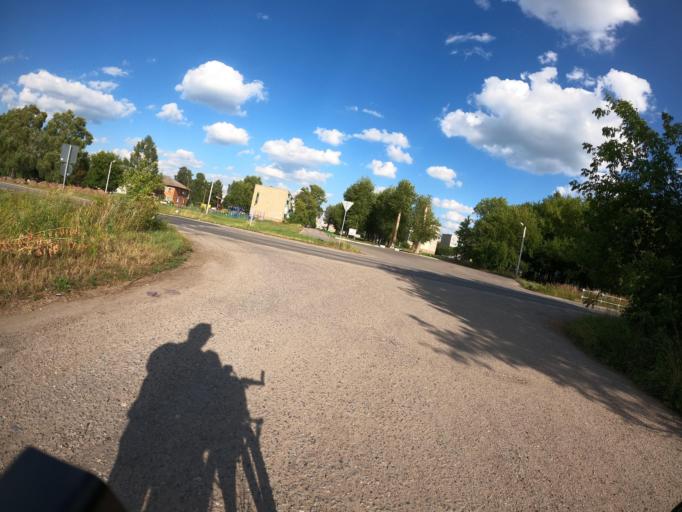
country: RU
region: Moskovskaya
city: Peski
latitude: 55.1945
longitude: 38.7403
